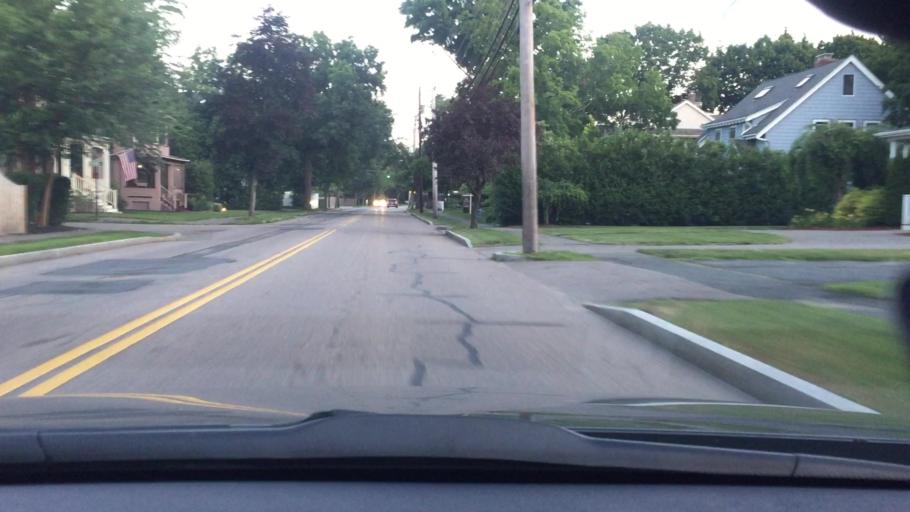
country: US
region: Massachusetts
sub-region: Norfolk County
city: Needham
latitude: 42.2817
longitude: -71.2299
